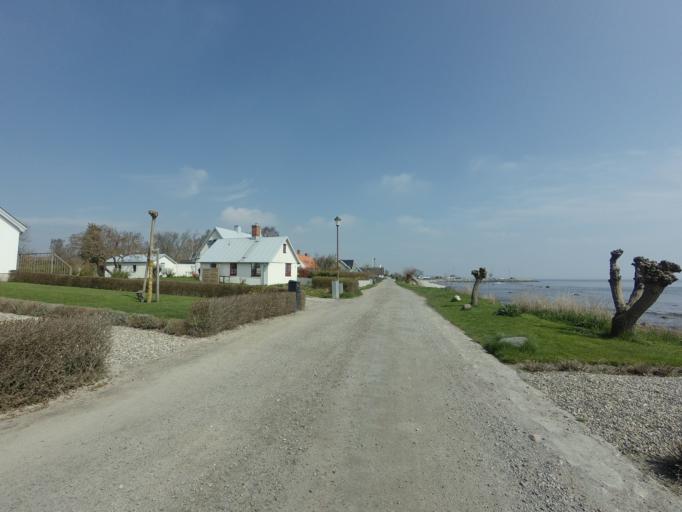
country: SE
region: Skane
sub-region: Skurups Kommun
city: Skivarp
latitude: 55.3919
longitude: 13.5984
